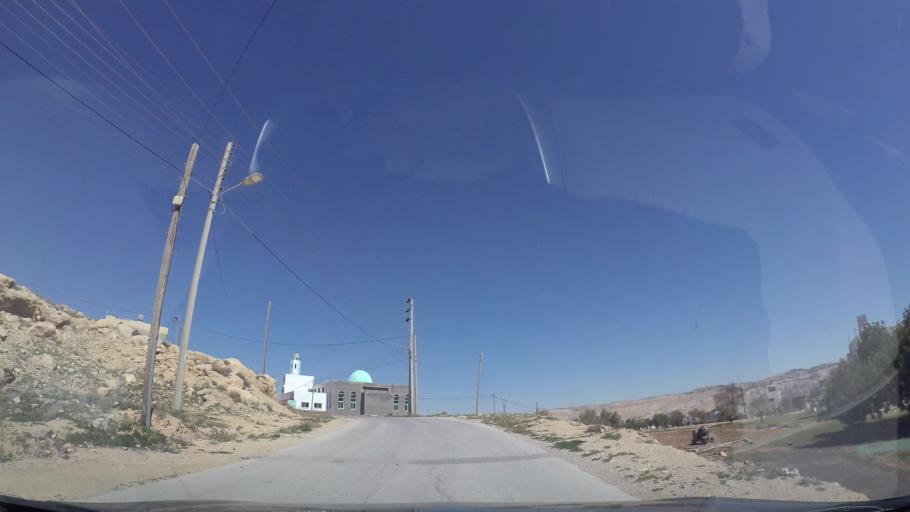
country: JO
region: Tafielah
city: At Tafilah
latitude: 30.8258
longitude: 35.5802
